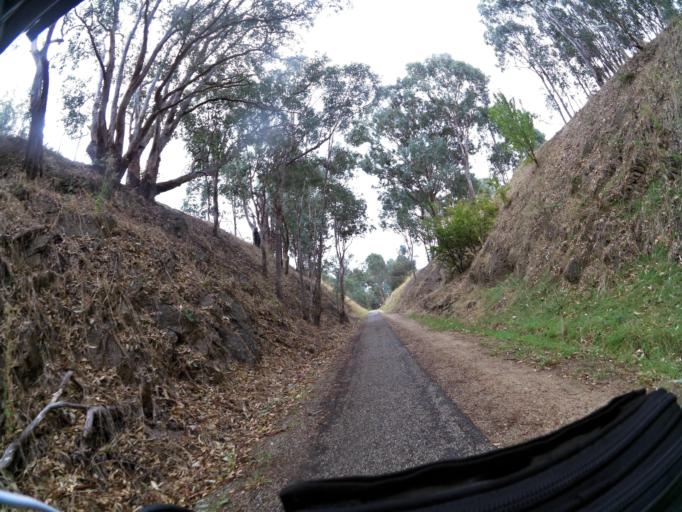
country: AU
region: New South Wales
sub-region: Albury Municipality
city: East Albury
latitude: -36.2251
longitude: 147.1209
